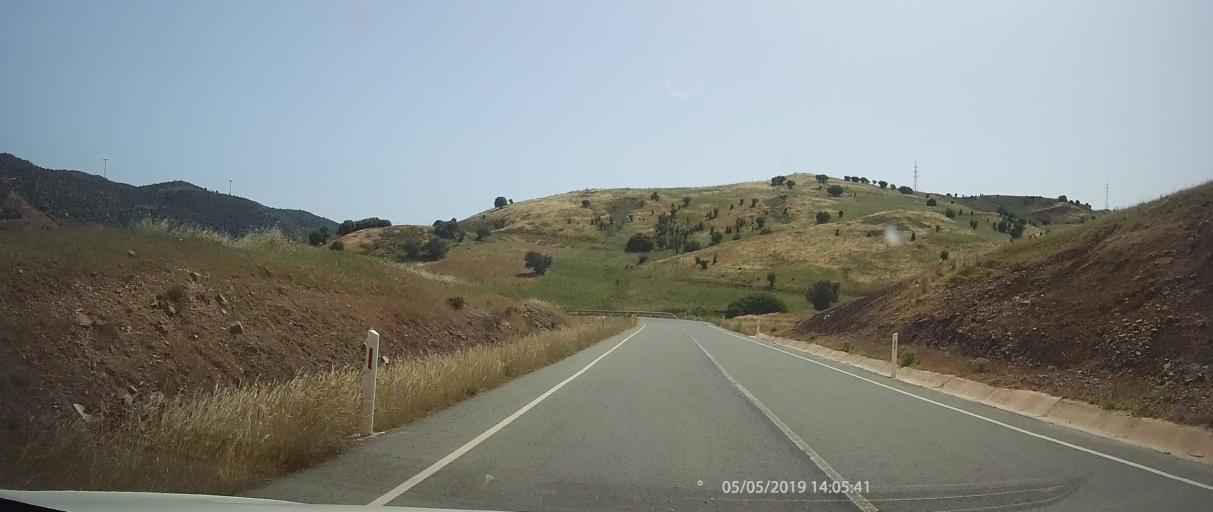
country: CY
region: Limassol
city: Pissouri
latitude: 34.7508
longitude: 32.6104
